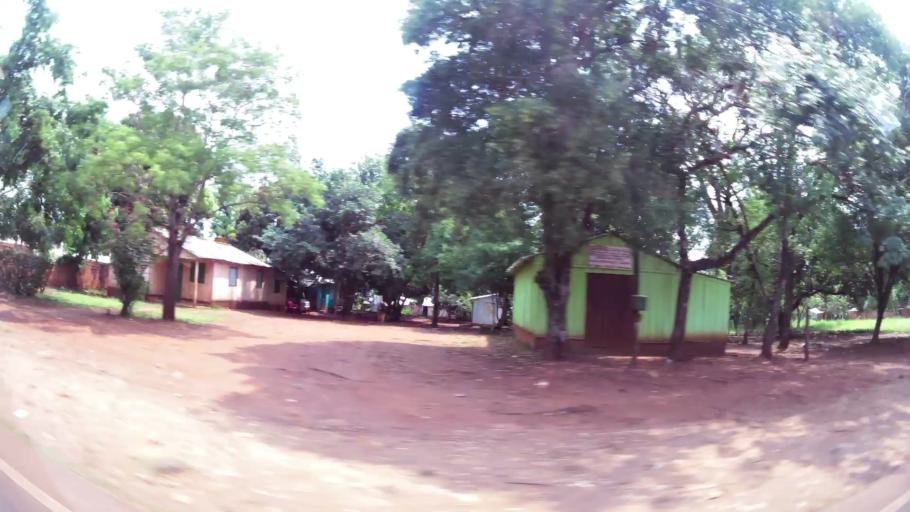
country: AR
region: Misiones
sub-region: Departamento de Iguazu
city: Puerto Iguazu
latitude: -25.5878
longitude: -54.6026
